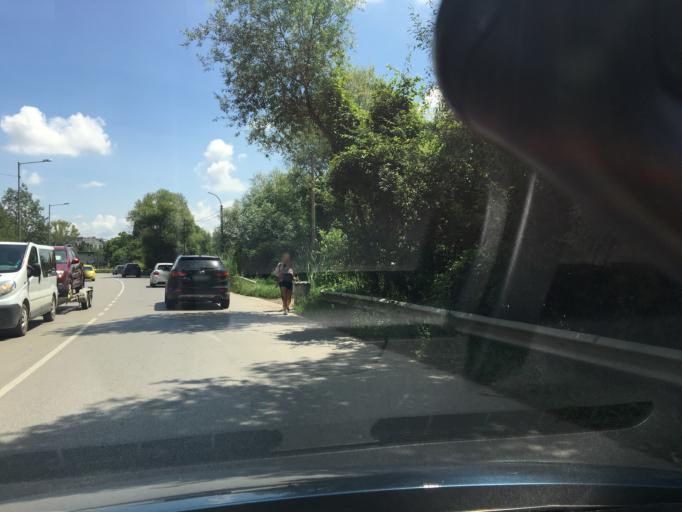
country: BG
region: Sofia-Capital
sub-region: Stolichna Obshtina
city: Sofia
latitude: 42.6582
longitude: 23.3073
